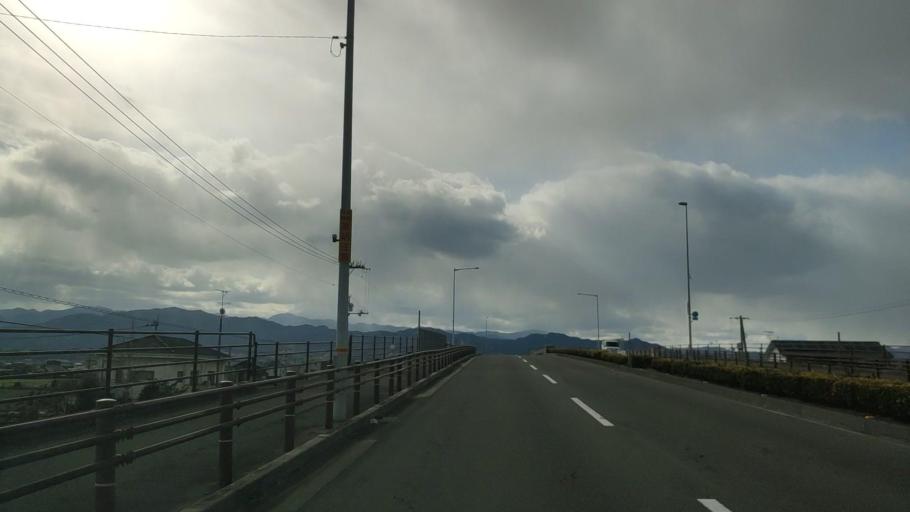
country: JP
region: Ehime
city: Saijo
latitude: 34.0453
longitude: 133.0058
